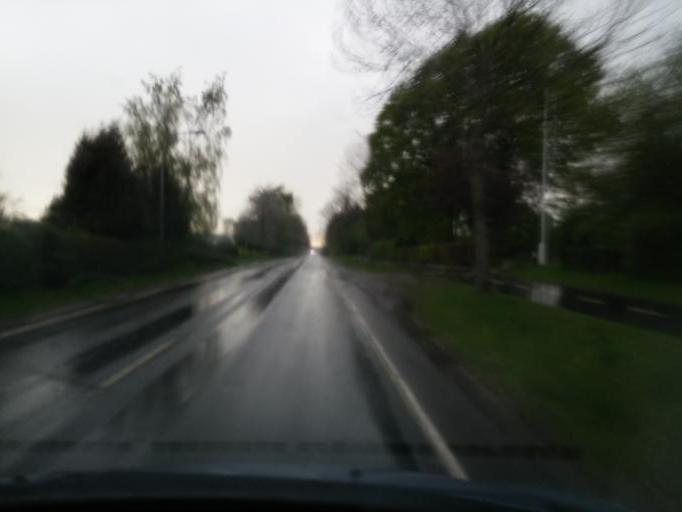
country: DK
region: South Denmark
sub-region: Odense Kommune
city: Bellinge
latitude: 55.3411
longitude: 10.2965
